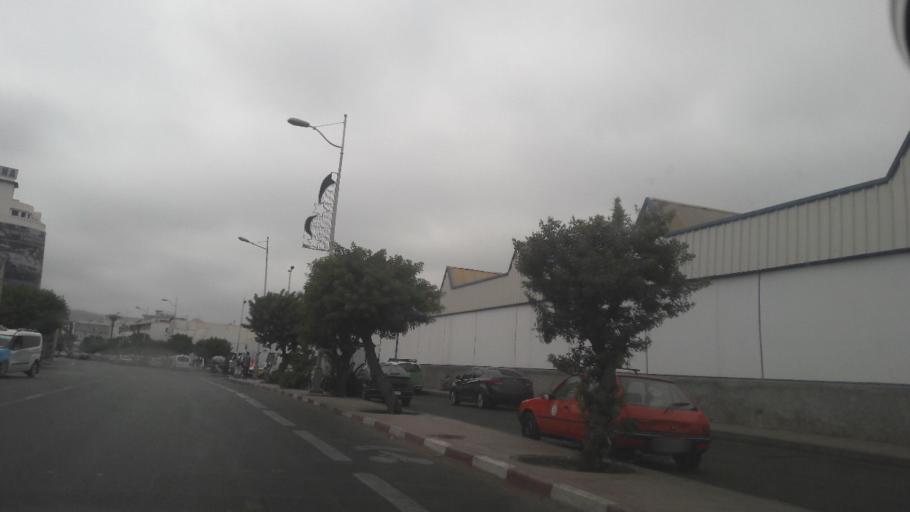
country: MA
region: Souss-Massa-Draa
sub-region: Agadir-Ida-ou-Tnan
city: Agadir
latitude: 30.4091
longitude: -9.5888
